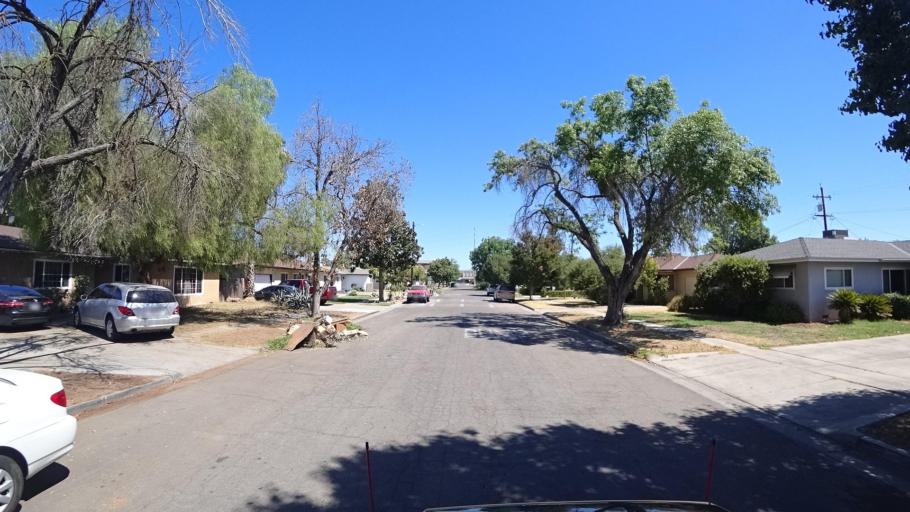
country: US
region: California
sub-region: Fresno County
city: Fresno
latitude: 36.7852
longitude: -119.7861
